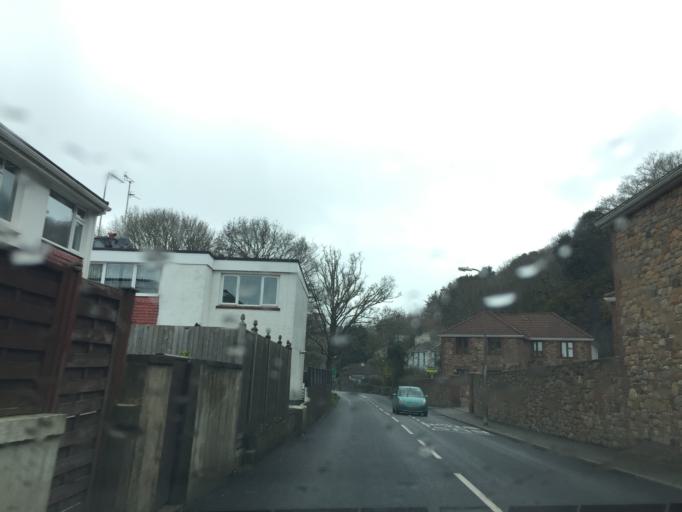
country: JE
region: St Helier
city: Saint Helier
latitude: 49.2038
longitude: -2.1551
